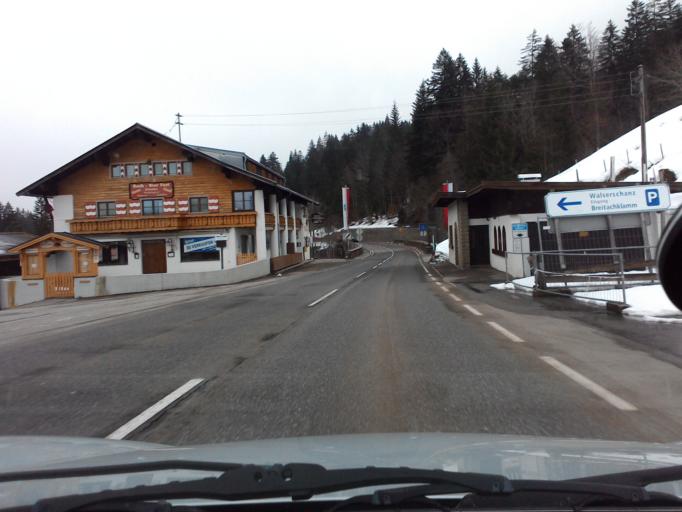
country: DE
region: Bavaria
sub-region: Swabia
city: Oberstdorf
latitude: 47.3866
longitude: 10.2290
